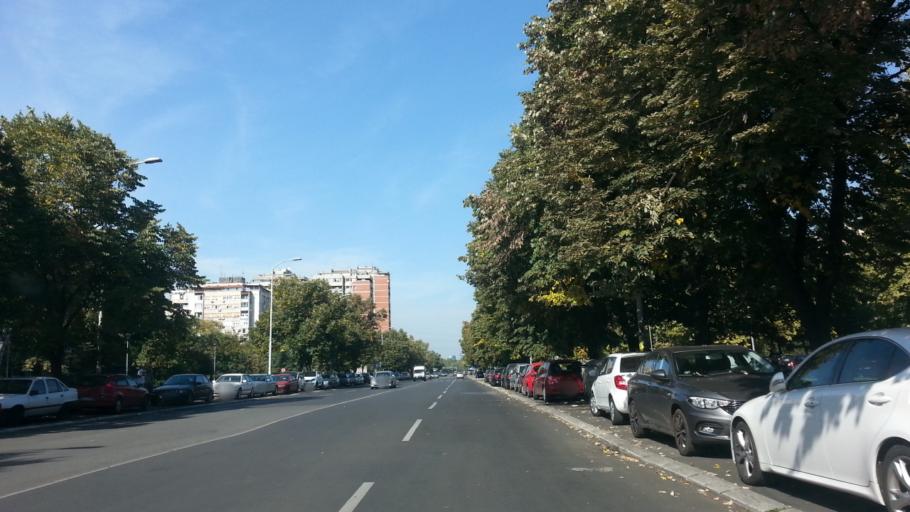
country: RS
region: Central Serbia
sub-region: Belgrade
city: Novi Beograd
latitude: 44.7992
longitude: 20.4001
